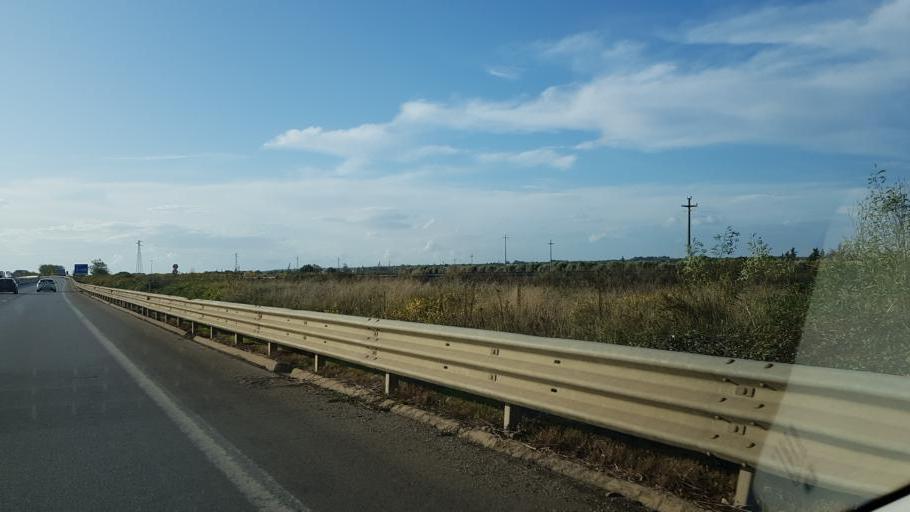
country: IT
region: Apulia
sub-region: Provincia di Brindisi
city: Francavilla Fontana
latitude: 40.5464
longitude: 17.5857
